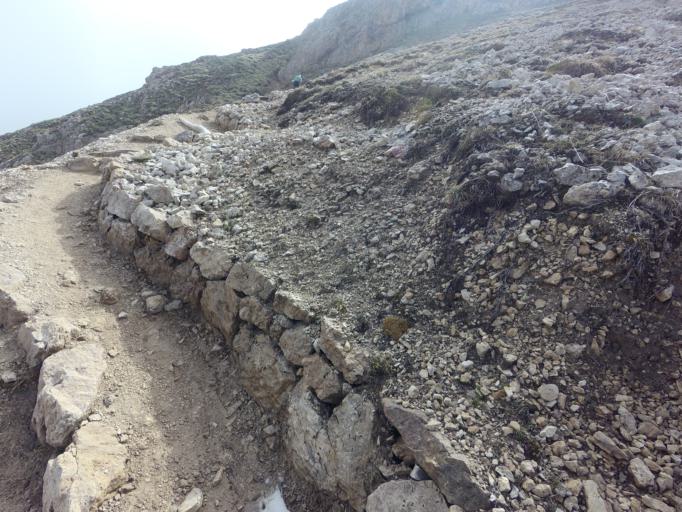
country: IT
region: Trentino-Alto Adige
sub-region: Provincia di Trento
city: Mazzin
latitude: 46.5030
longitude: 11.6362
